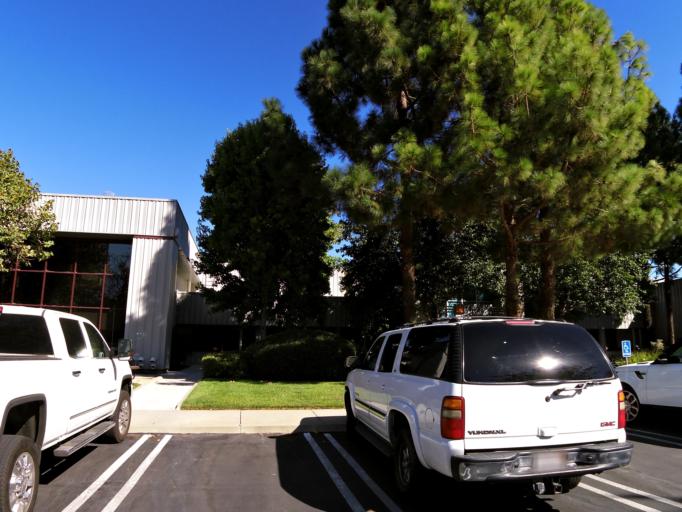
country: US
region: California
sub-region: San Luis Obispo County
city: San Luis Obispo
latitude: 35.2494
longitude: -120.6713
